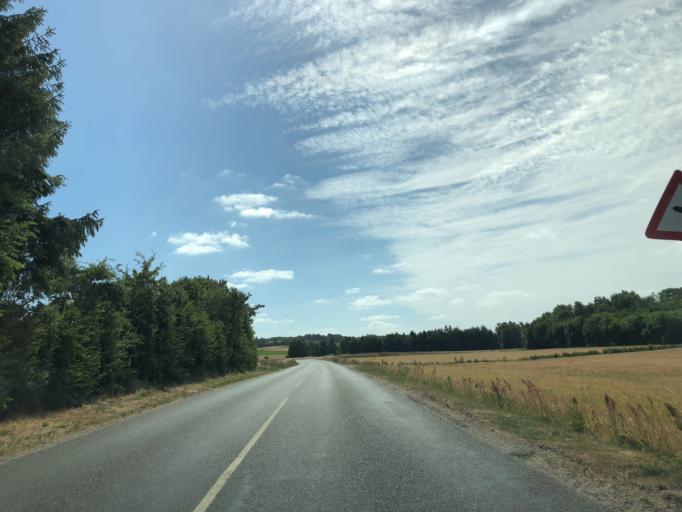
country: DK
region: North Denmark
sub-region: Vesthimmerland Kommune
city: Alestrup
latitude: 56.5767
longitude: 9.5141
